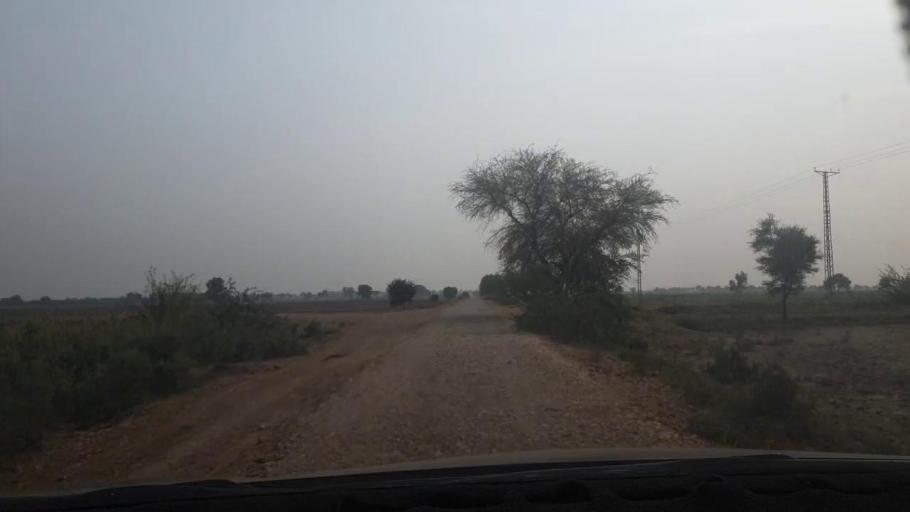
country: PK
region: Sindh
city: Jamshoro
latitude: 25.5207
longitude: 68.3146
